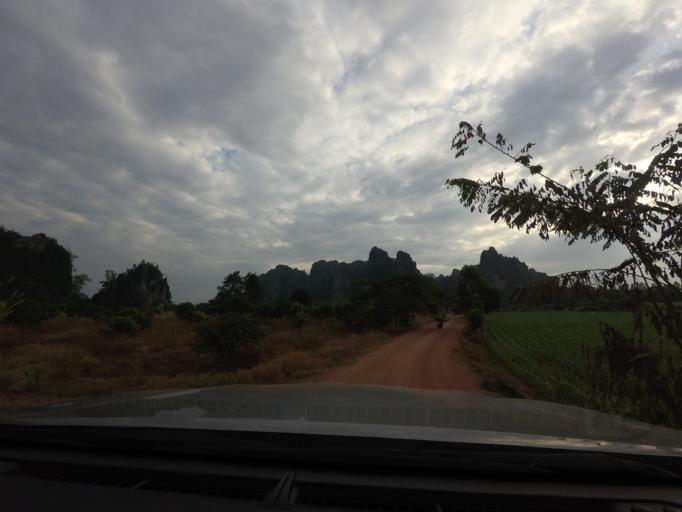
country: TH
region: Phitsanulok
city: Noen Maprang
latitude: 16.5799
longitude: 100.6845
